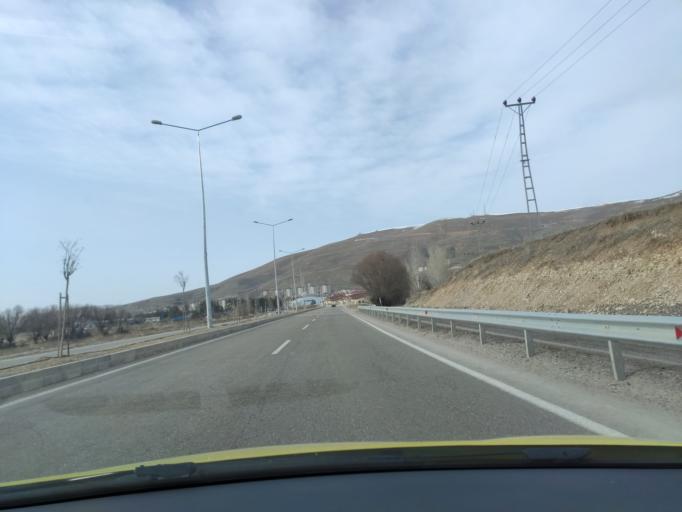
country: TR
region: Bayburt
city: Bayburt
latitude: 40.2289
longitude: 40.2578
